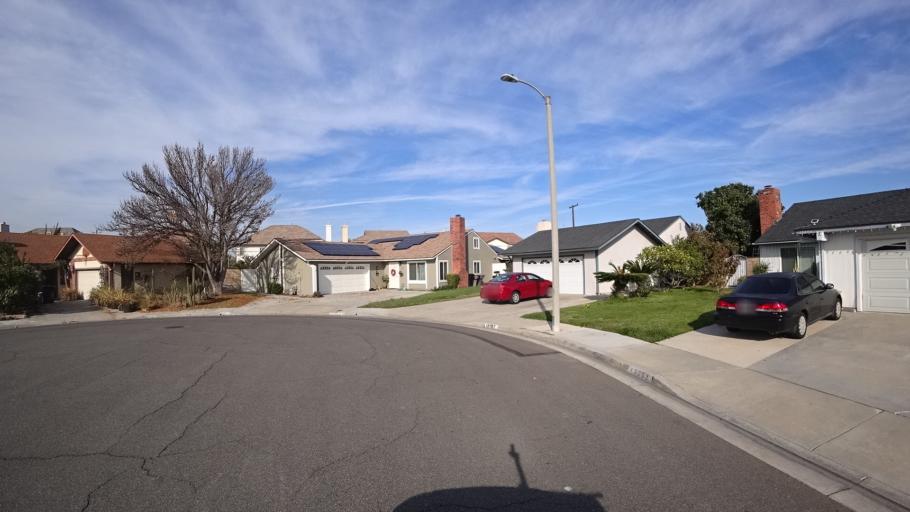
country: US
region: California
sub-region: Orange County
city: Garden Grove
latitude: 33.7713
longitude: -117.9046
